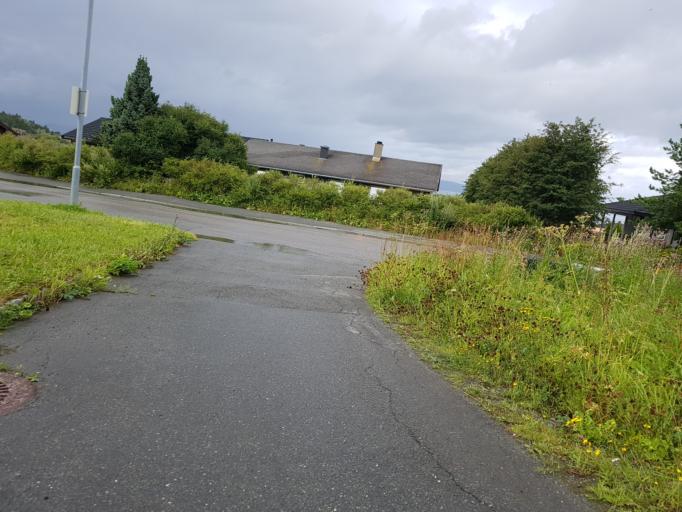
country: NO
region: Sor-Trondelag
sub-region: Trondheim
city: Trondheim
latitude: 63.4108
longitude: 10.4845
